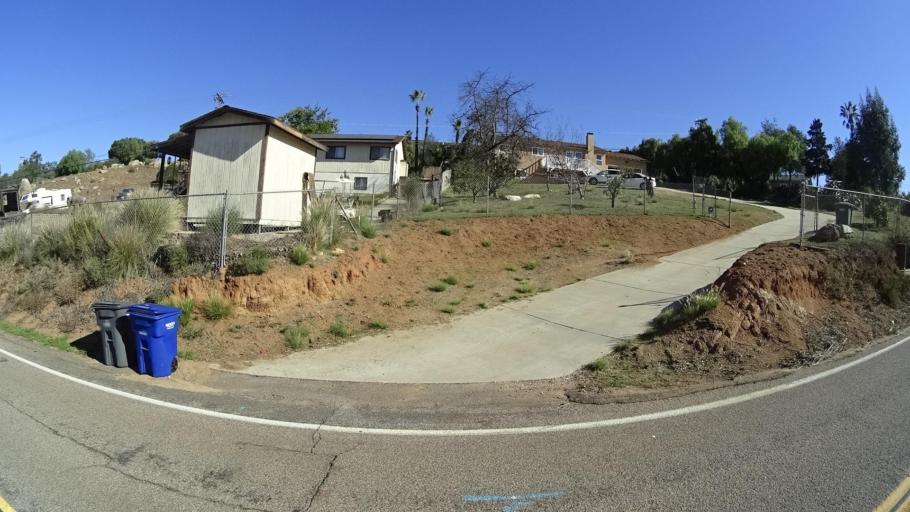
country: US
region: California
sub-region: San Diego County
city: Jamul
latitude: 32.7301
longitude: -116.8495
